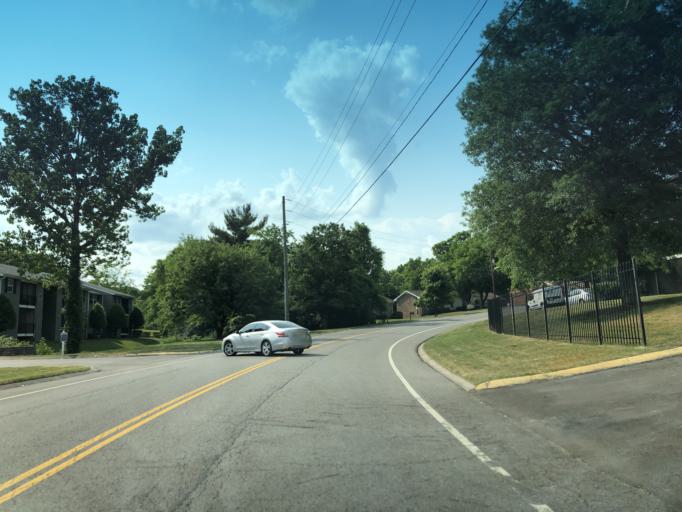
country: US
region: Tennessee
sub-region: Davidson County
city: Goodlettsville
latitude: 36.2652
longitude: -86.7246
